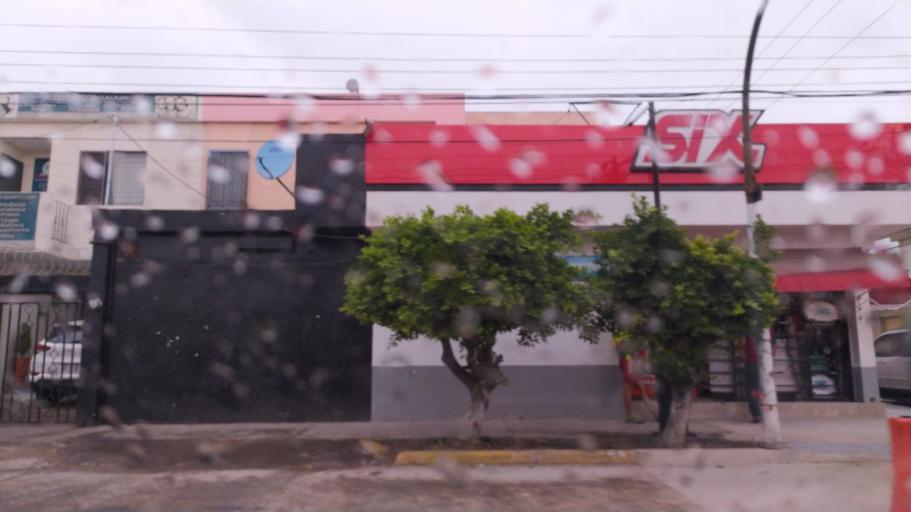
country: MX
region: Jalisco
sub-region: Zapopan
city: Zapopan
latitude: 20.7164
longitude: -103.3615
